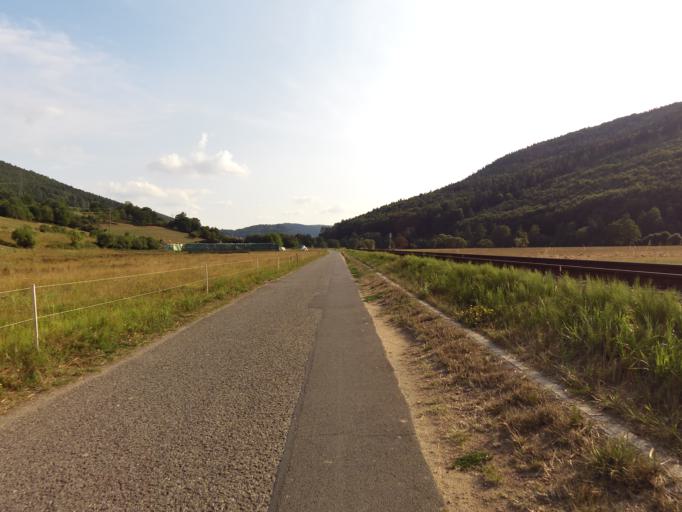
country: DE
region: Bavaria
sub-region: Regierungsbezirk Unterfranken
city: Weilbach
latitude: 49.6843
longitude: 9.2221
